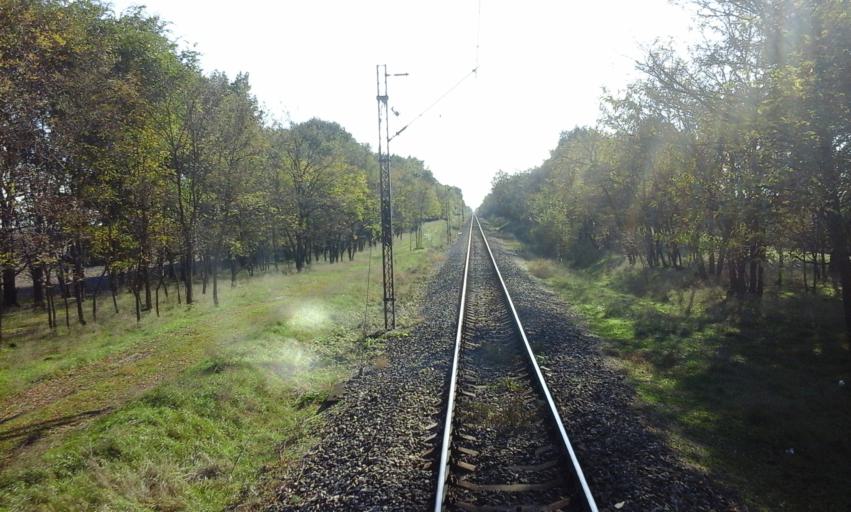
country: RS
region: Autonomna Pokrajina Vojvodina
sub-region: Severnobacki Okrug
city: Backa Topola
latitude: 45.8678
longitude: 19.6572
